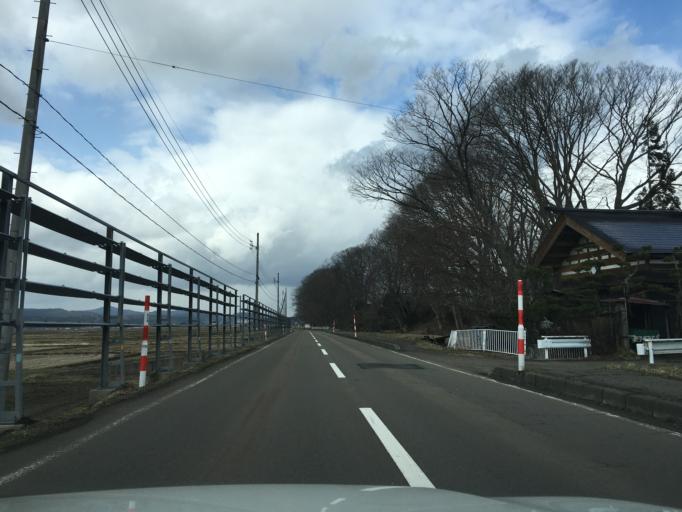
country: JP
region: Akita
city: Takanosu
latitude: 40.1442
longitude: 140.3466
